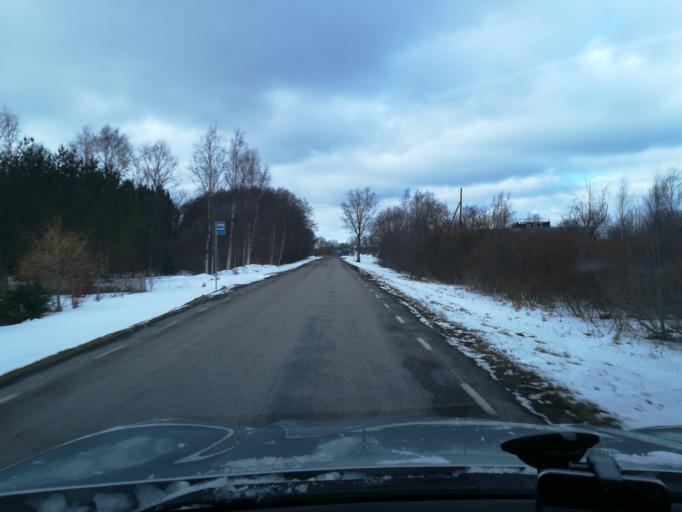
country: EE
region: Harju
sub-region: Keila linn
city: Keila
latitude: 59.4445
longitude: 24.3831
